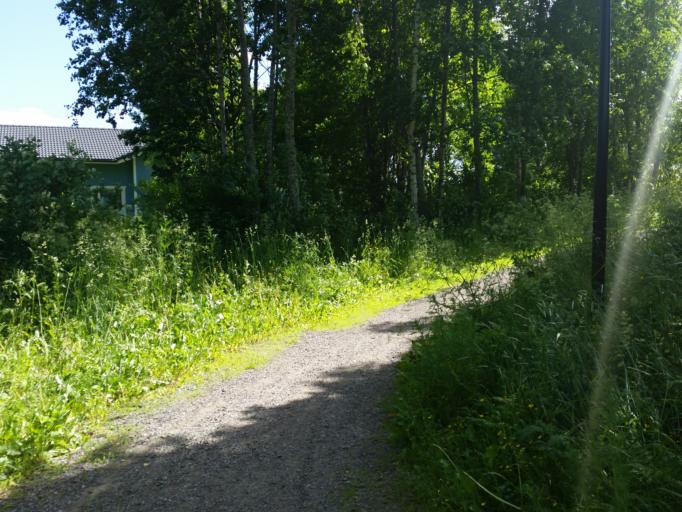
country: FI
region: Northern Savo
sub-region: Varkaus
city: Varkaus
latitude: 62.3373
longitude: 27.9034
